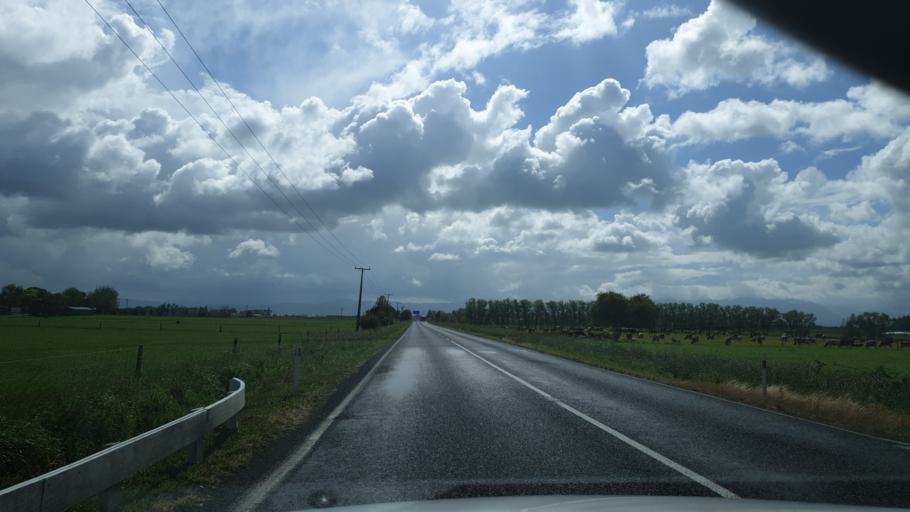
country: NZ
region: Waikato
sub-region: Hauraki District
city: Paeroa
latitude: -37.5127
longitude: 175.5156
